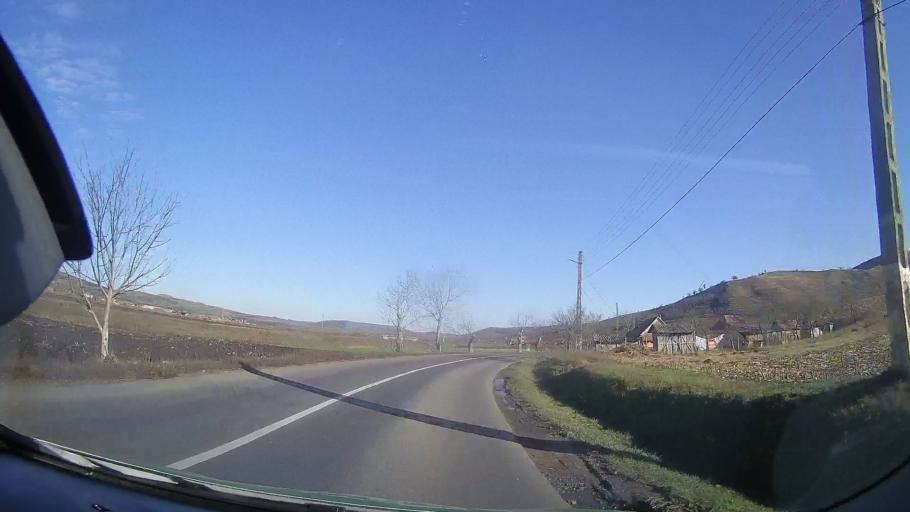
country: RO
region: Mures
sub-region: Comuna Grebenisu de Campie
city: Grebenisu de Campie
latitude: 46.5616
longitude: 24.3349
